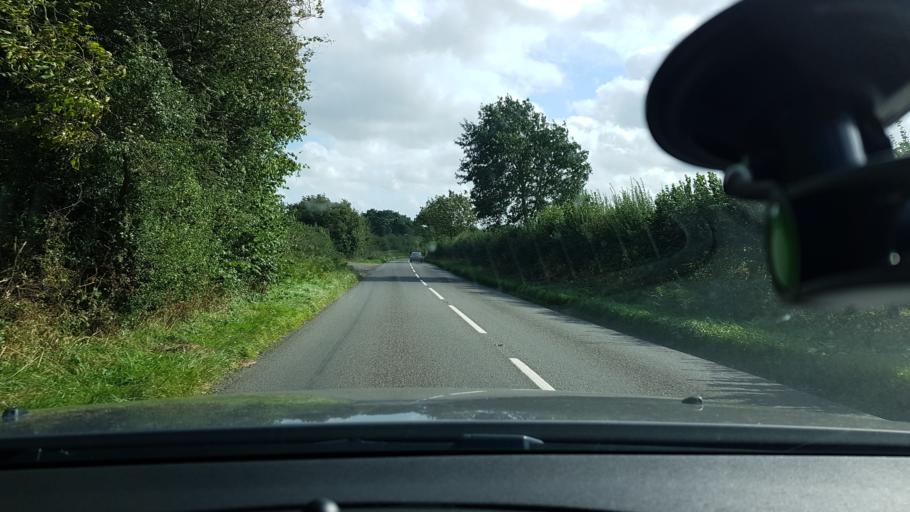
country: GB
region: England
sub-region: West Berkshire
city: Lambourn
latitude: 51.4872
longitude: -1.5485
